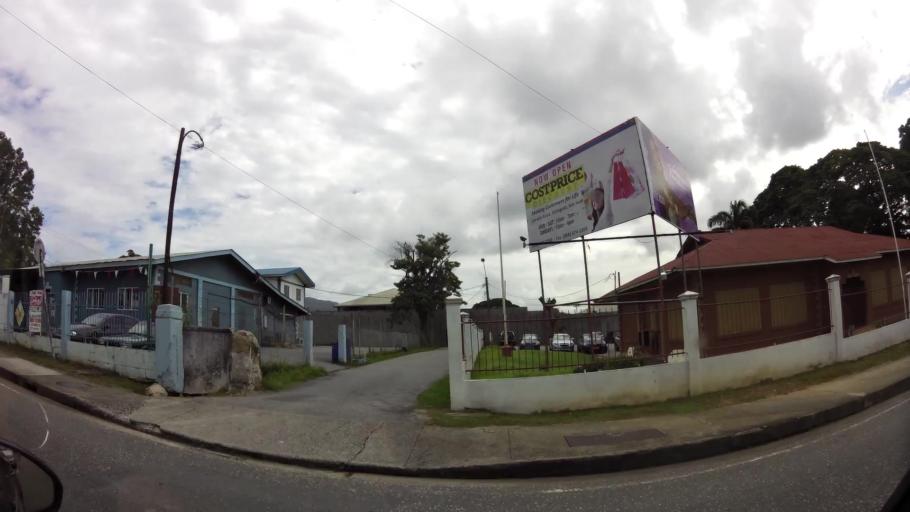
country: TT
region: City of Port of Spain
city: Port-of-Spain
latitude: 10.6738
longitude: -61.5293
